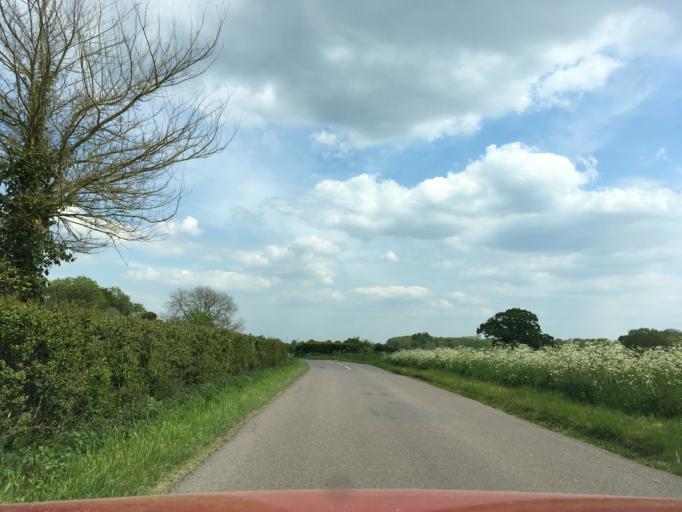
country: GB
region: England
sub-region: South Gloucestershire
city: Thornbury
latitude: 51.6273
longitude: -2.5485
